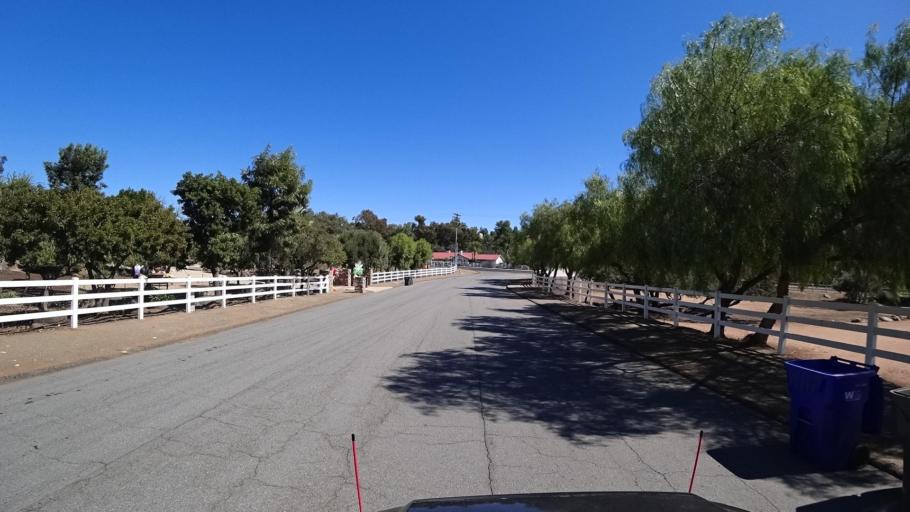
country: US
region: California
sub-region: San Diego County
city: Alpine
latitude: 32.8140
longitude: -116.7781
